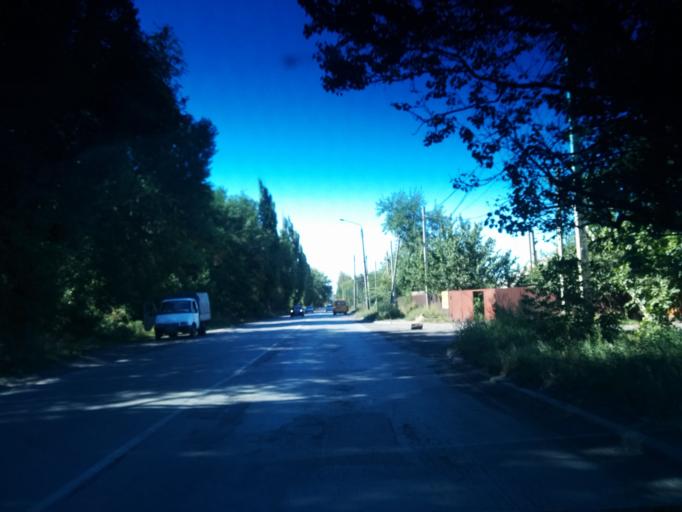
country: RU
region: Rostov
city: Shakhty
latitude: 47.6803
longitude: 40.2811
